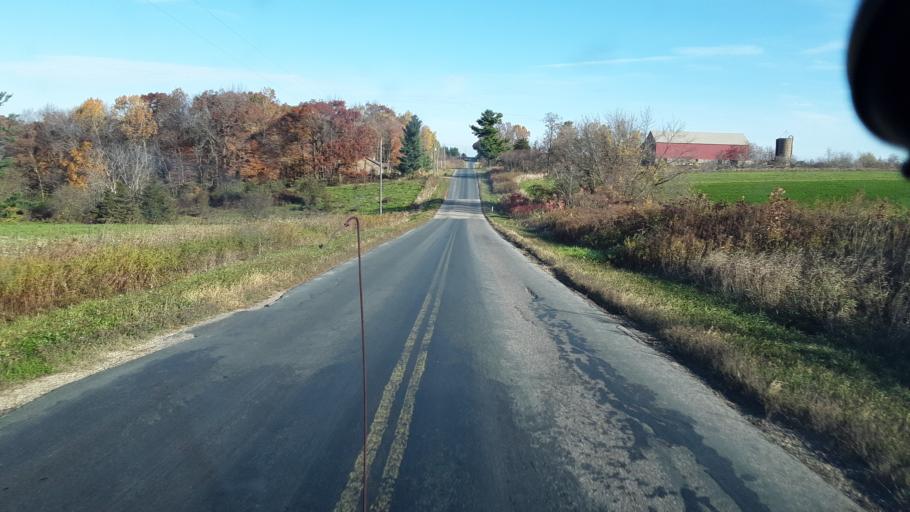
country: US
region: Wisconsin
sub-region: Vernon County
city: Hillsboro
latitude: 43.7789
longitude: -90.4433
